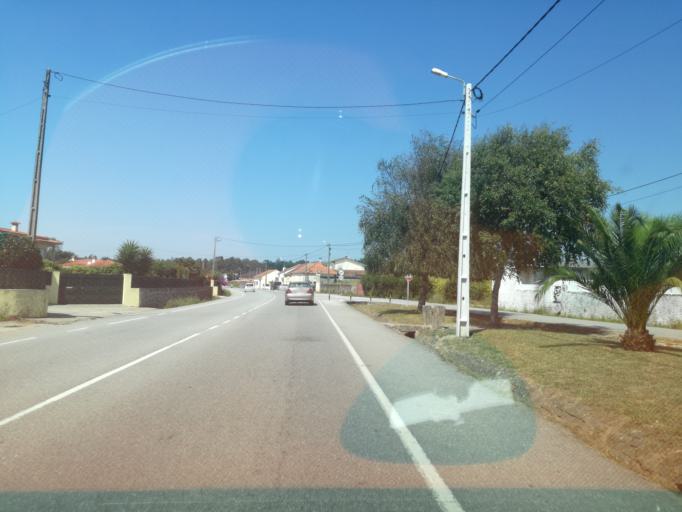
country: PT
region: Braga
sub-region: Esposende
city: Apulia
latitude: 41.4763
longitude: -8.7464
